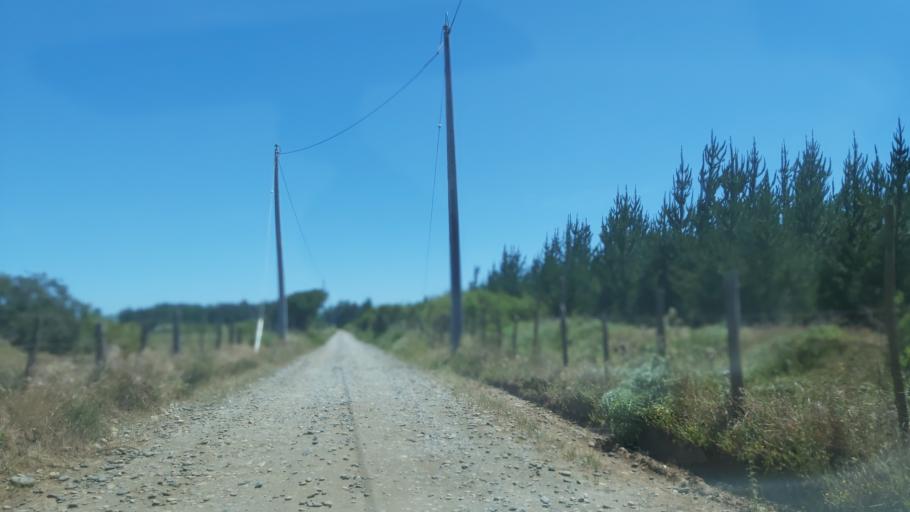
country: CL
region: Maule
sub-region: Provincia de Talca
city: Constitucion
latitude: -35.1655
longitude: -72.2631
